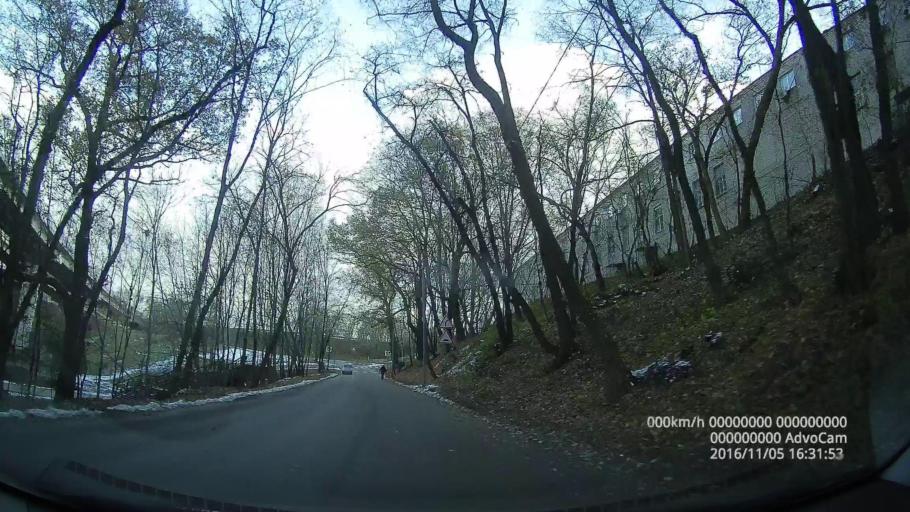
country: RU
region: Voronezj
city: Voronezh
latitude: 51.6893
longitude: 39.2198
